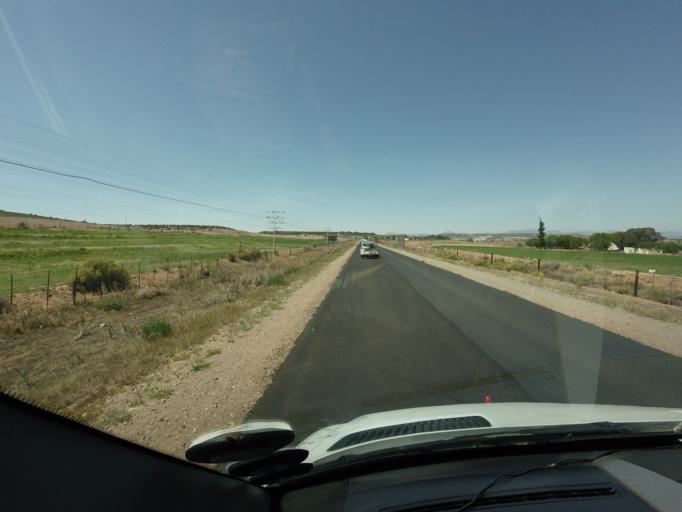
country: ZA
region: Western Cape
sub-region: Eden District Municipality
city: Oudtshoorn
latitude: -33.5197
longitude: 22.2439
